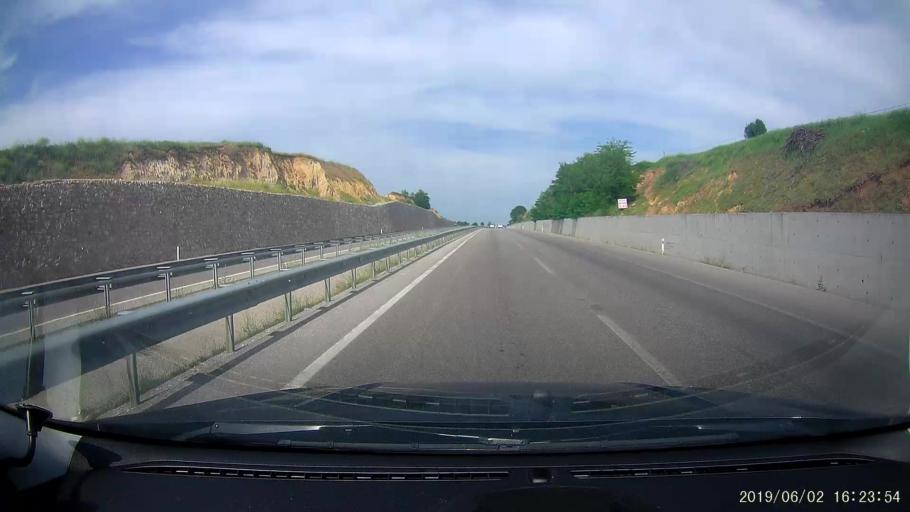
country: TR
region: Samsun
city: Havza
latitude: 40.9962
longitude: 35.7461
